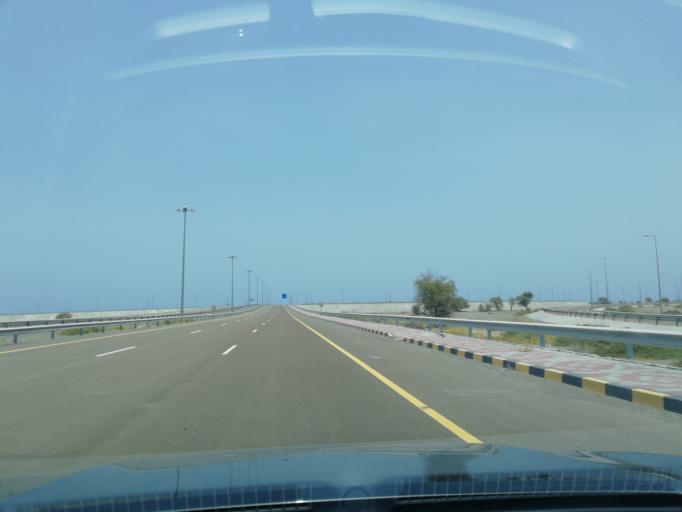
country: AE
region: Al Fujayrah
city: Al Fujayrah
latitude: 24.9516
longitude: 56.3662
